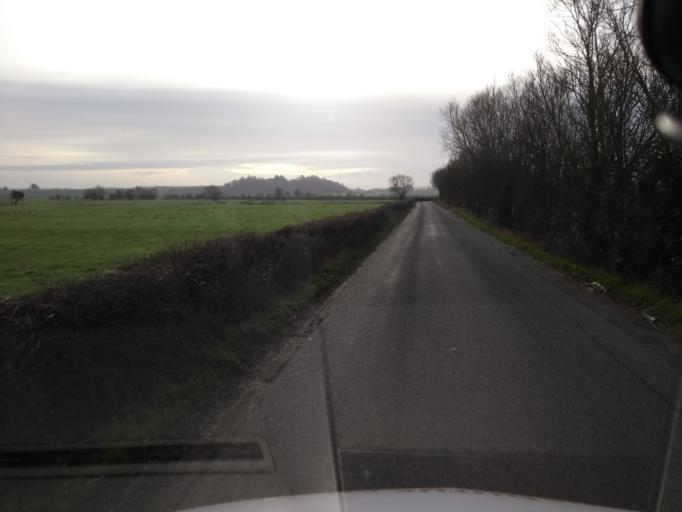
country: GB
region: England
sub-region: Somerset
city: Creech Saint Michael
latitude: 51.0411
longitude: -2.9777
